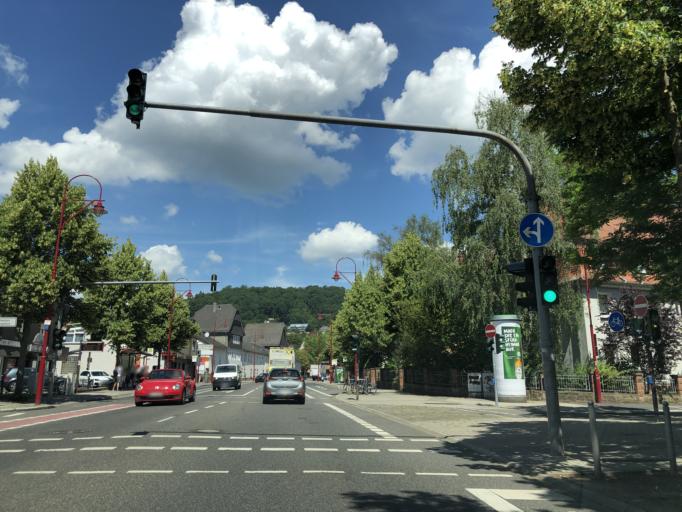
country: DE
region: Hesse
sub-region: Regierungsbezirk Giessen
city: Marburg an der Lahn
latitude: 50.8006
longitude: 8.7605
